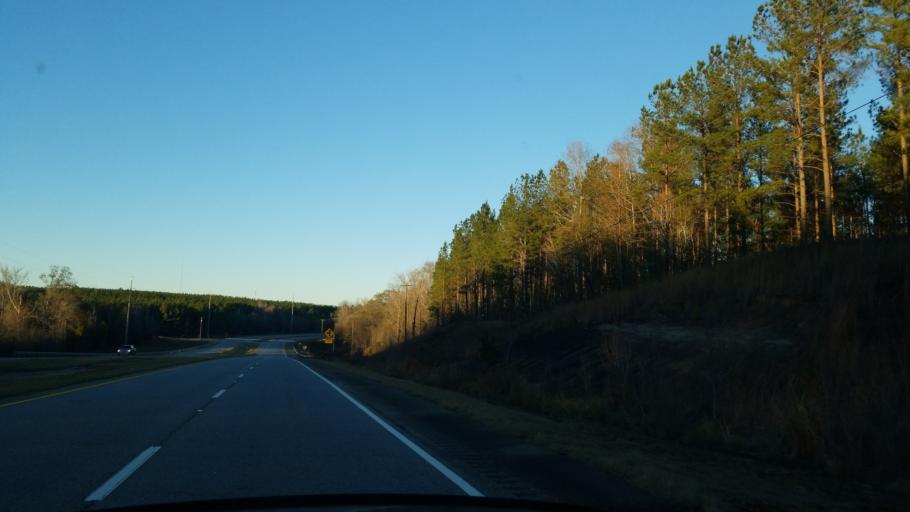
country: US
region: Georgia
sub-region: Chattahoochee County
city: Cusseta
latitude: 32.2656
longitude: -84.7858
